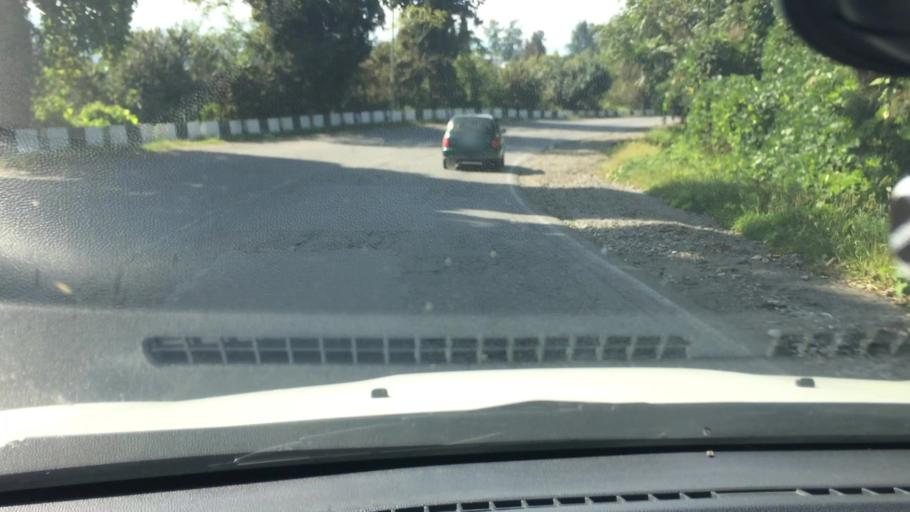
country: GE
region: Ajaria
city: Kobuleti
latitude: 41.7531
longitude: 41.7475
